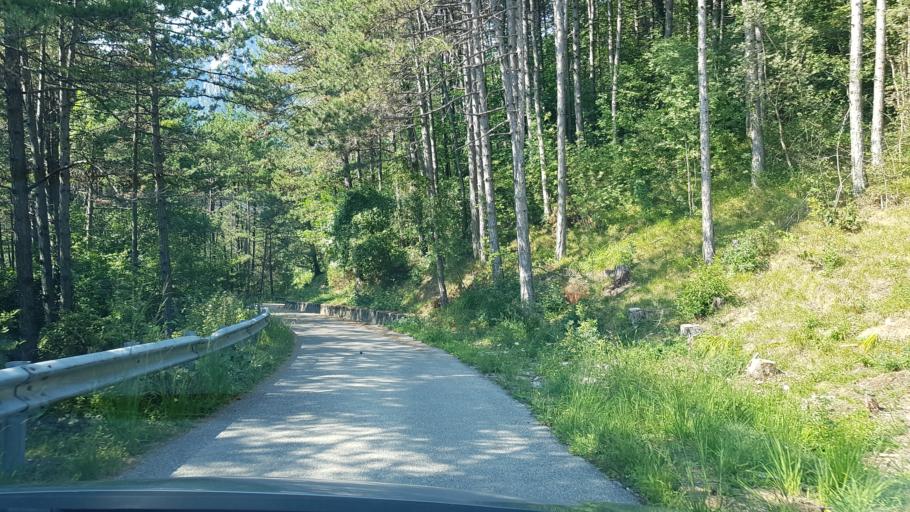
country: IT
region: Friuli Venezia Giulia
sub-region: Provincia di Udine
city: Moggio Udinese
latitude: 46.4329
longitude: 13.2054
